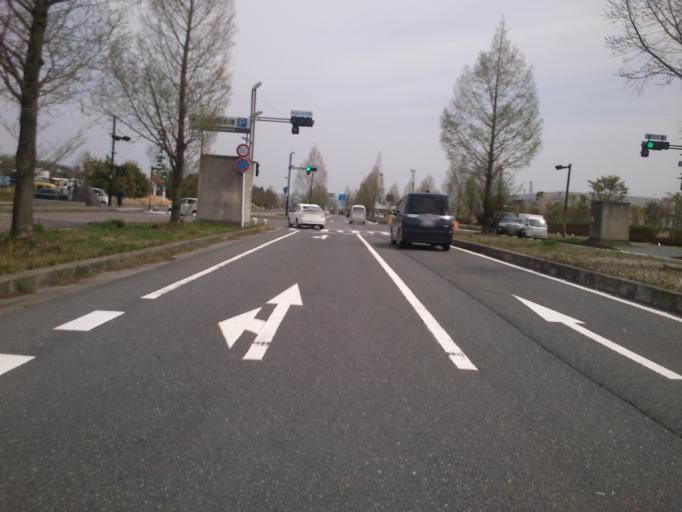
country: JP
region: Nara
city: Nara-shi
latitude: 34.7449
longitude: 135.7711
